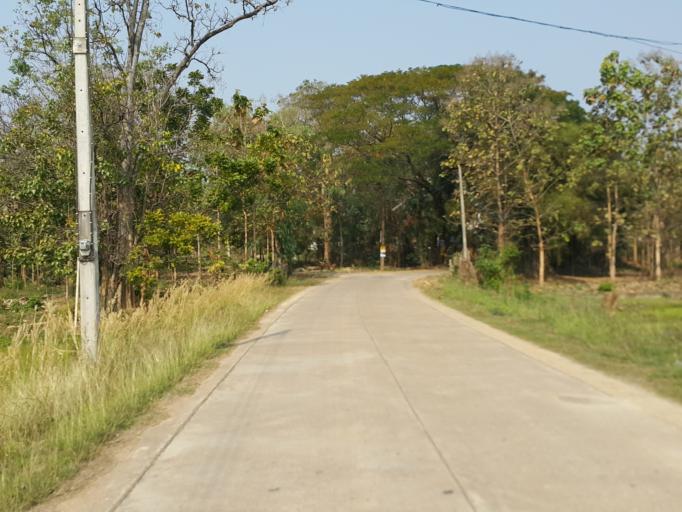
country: TH
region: Sukhothai
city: Thung Saliam
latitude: 17.3304
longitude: 99.5351
